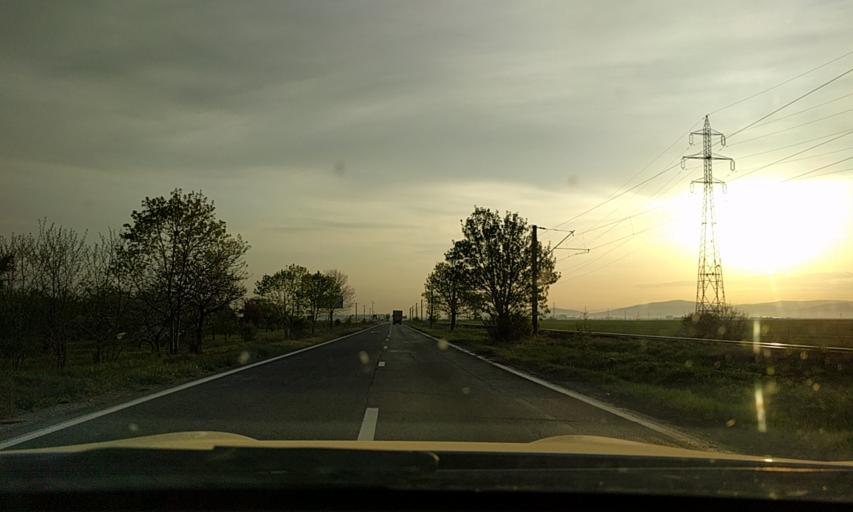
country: RO
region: Brasov
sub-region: Comuna Harman
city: Harman
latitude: 45.7111
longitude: 25.7070
